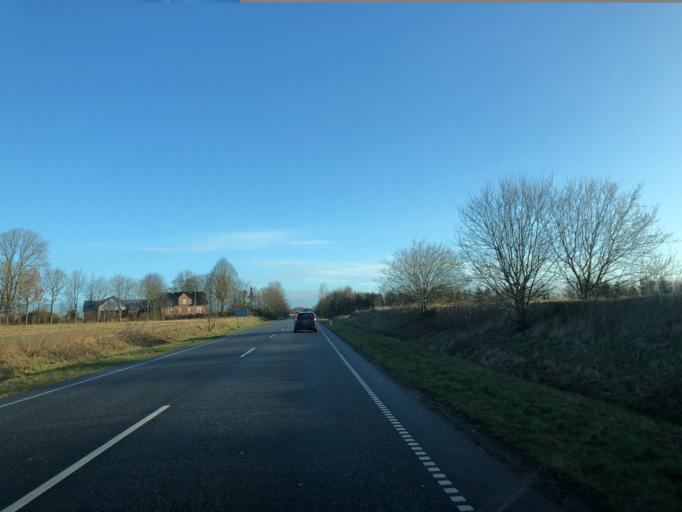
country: DK
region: Central Jutland
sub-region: Arhus Kommune
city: Framlev
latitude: 56.1878
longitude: 10.0057
